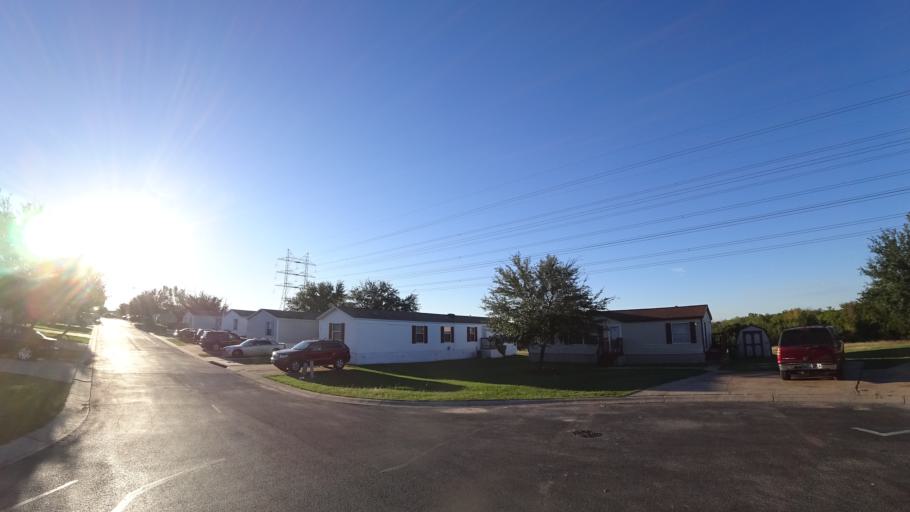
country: US
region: Texas
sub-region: Travis County
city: Manor
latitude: 30.3118
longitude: -97.6287
